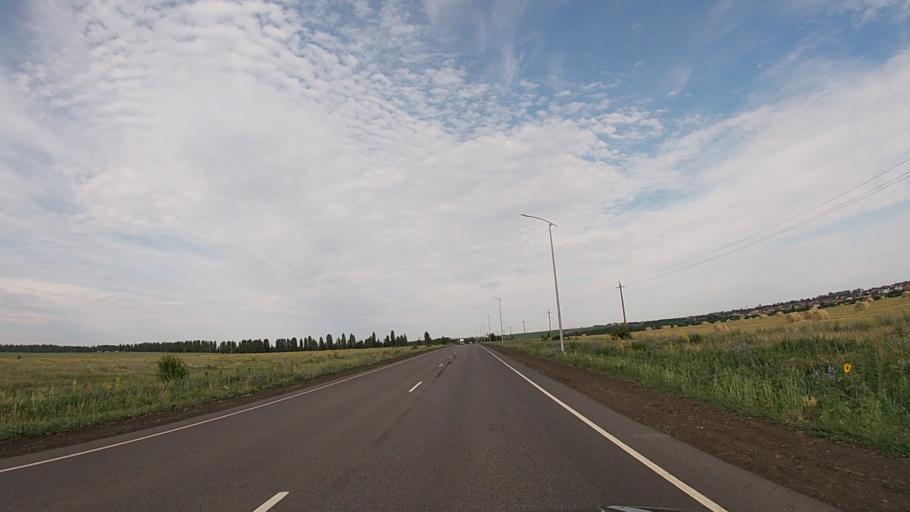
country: RU
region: Belgorod
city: Severnyy
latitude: 50.6660
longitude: 36.5359
